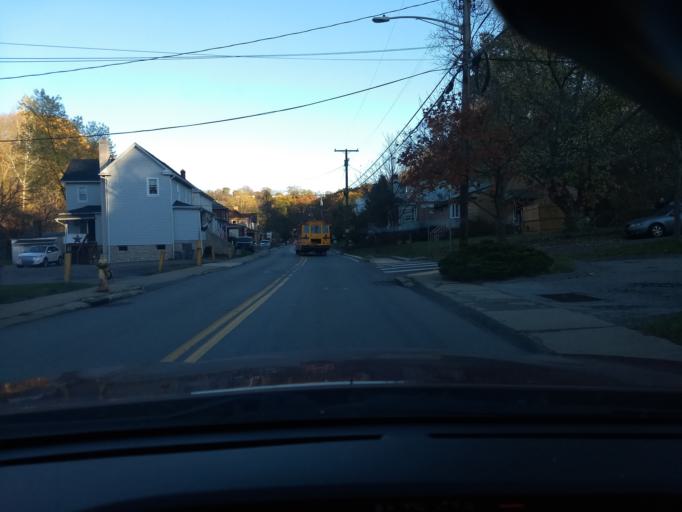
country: US
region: Pennsylvania
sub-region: Allegheny County
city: Bridgeville
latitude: 40.3549
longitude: -80.1054
